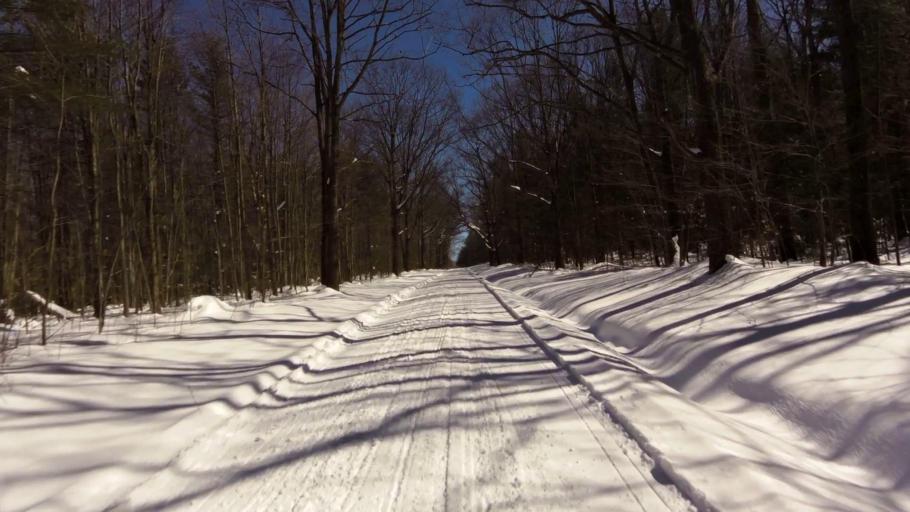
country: US
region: New York
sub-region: Allegany County
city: Cuba
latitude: 42.3267
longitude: -78.2372
